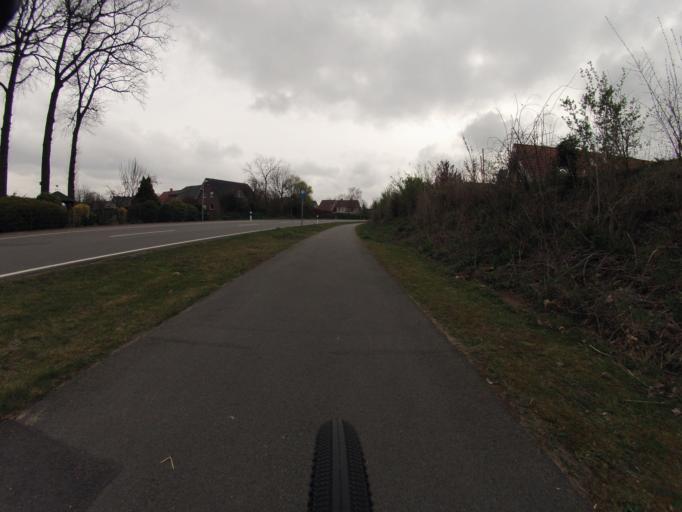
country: DE
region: North Rhine-Westphalia
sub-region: Regierungsbezirk Munster
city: Mettingen
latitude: 52.3291
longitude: 7.7773
